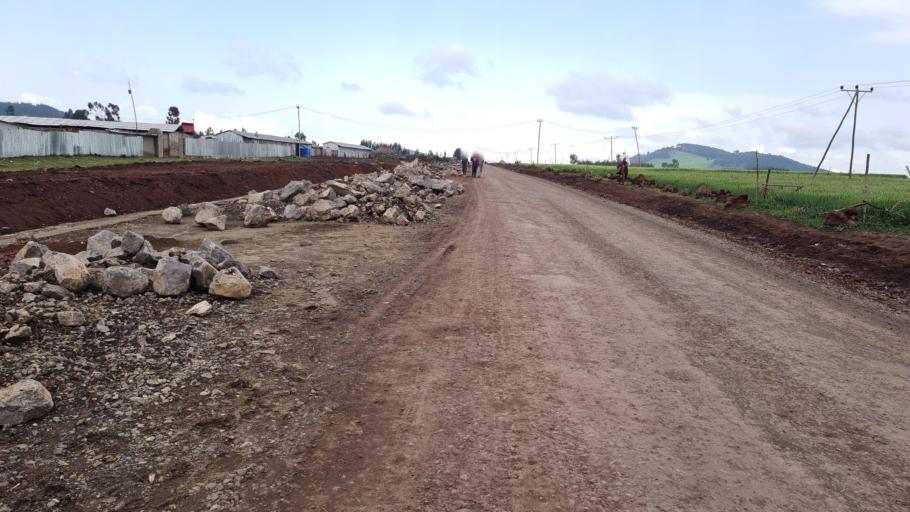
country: ET
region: Oromiya
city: Huruta
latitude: 8.0799
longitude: 39.5449
